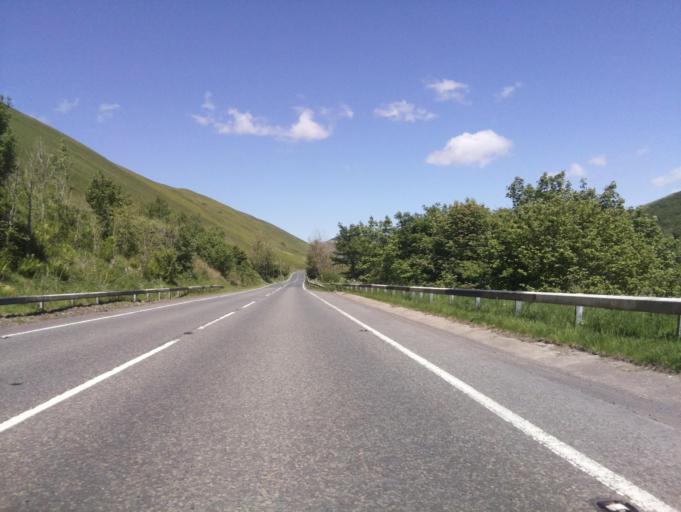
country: GB
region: Scotland
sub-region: Dumfries and Galloway
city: Langholm
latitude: 55.2344
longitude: -2.9758
